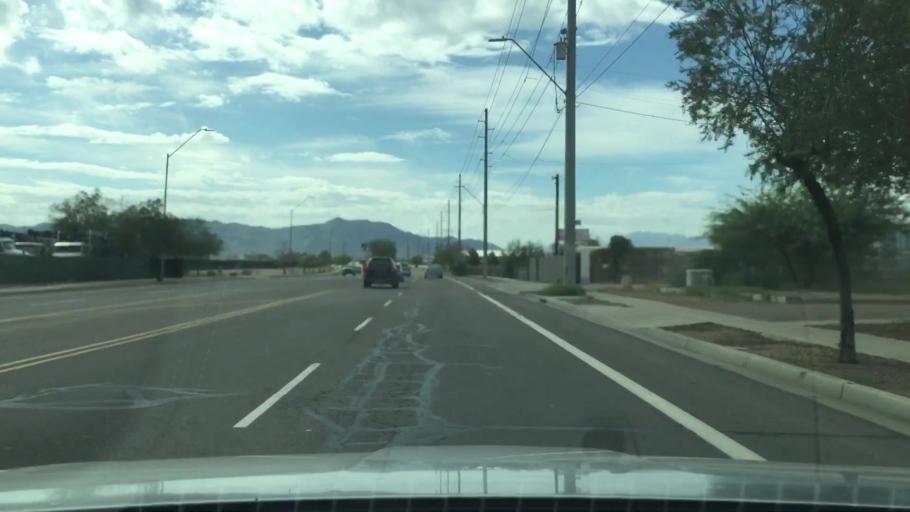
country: US
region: Arizona
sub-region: Maricopa County
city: Laveen
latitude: 33.4192
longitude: -112.1346
